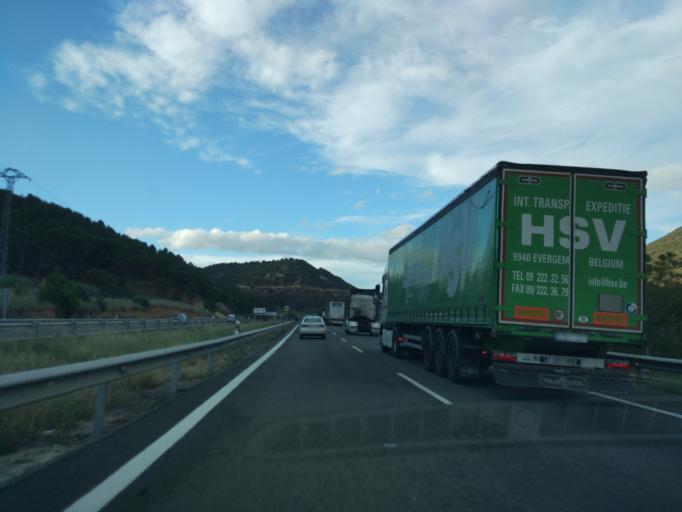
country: ES
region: Castille-La Mancha
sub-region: Provincia de Guadalajara
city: Tortola de Henares
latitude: 40.6922
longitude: -3.0861
